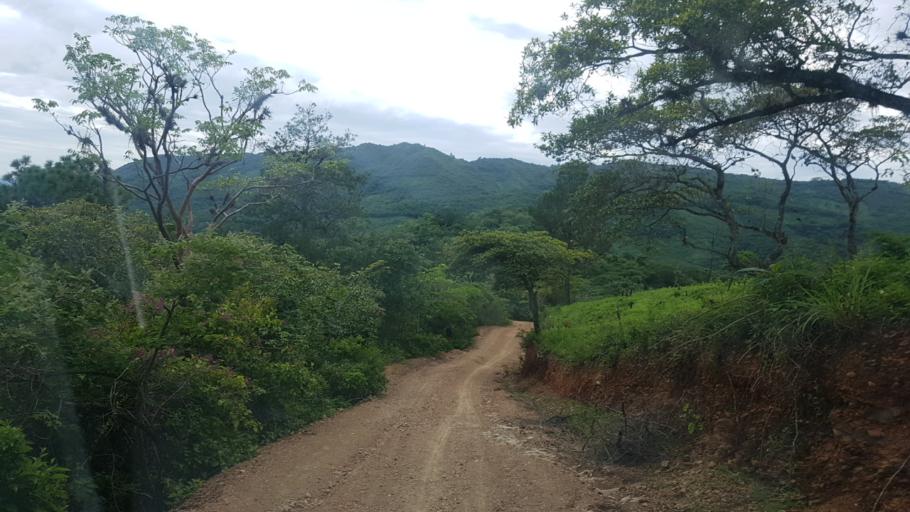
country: NI
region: Nueva Segovia
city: Mozonte
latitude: 13.5903
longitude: -86.4118
